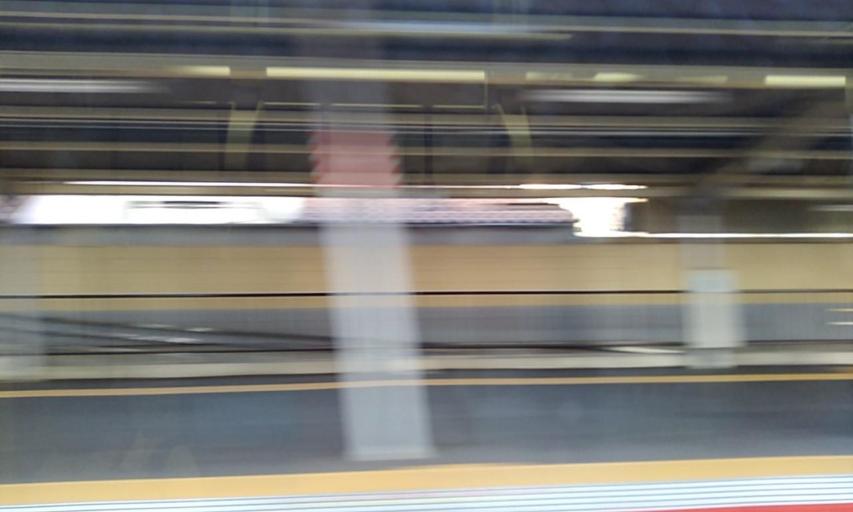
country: JP
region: Osaka
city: Sakai
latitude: 34.6060
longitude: 135.4969
